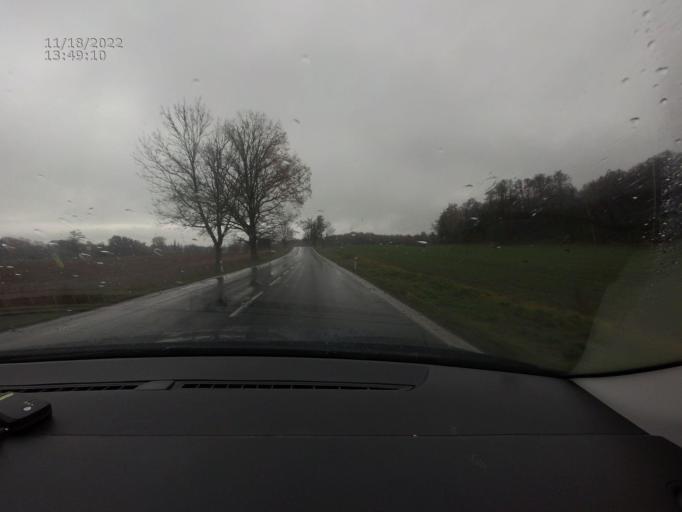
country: CZ
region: Jihocesky
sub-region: Okres Strakonice
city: Blatna
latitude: 49.4146
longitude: 13.8928
